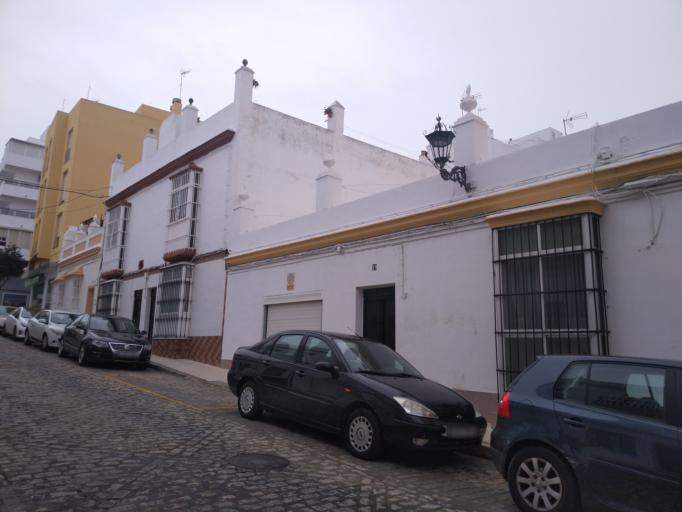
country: ES
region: Andalusia
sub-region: Provincia de Cadiz
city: San Fernando
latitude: 36.4708
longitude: -6.1966
